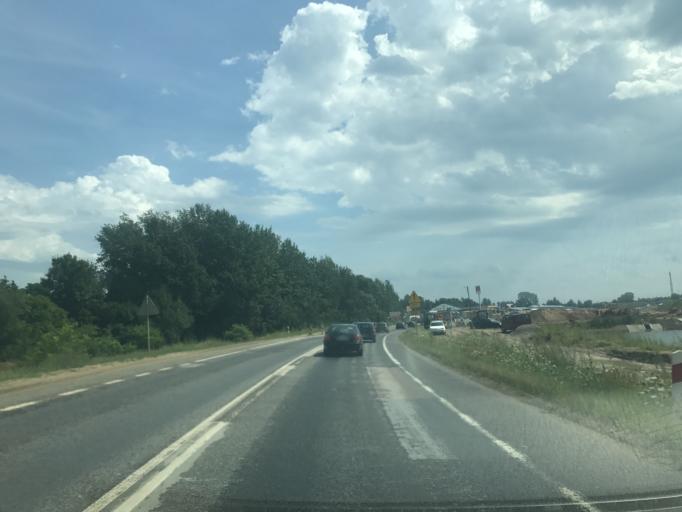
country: PL
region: Warmian-Masurian Voivodeship
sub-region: Powiat ostrodzki
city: Ostroda
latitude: 53.7116
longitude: 19.9744
